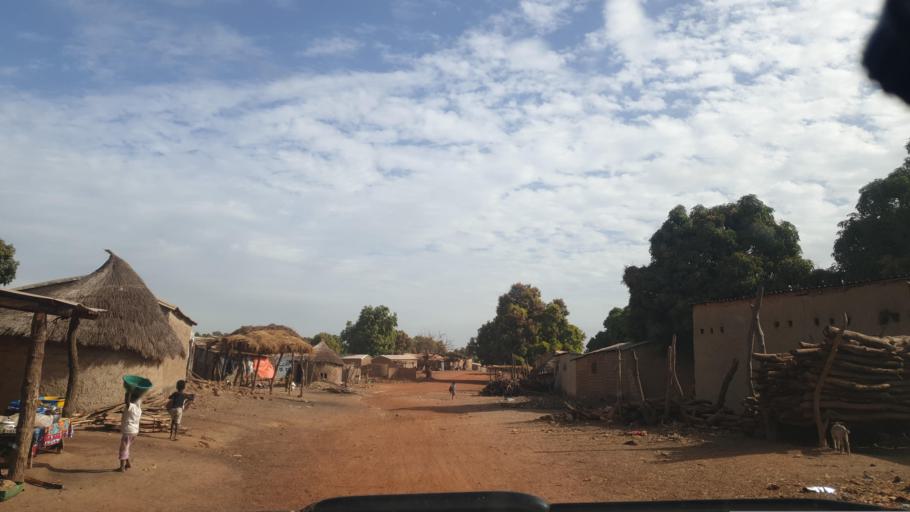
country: ML
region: Sikasso
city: Yanfolila
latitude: 11.4169
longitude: -7.9996
